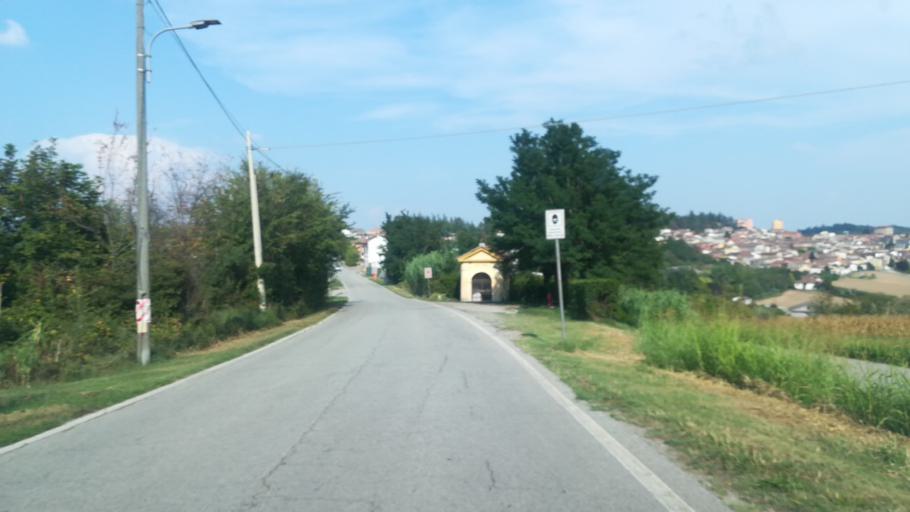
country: IT
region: Piedmont
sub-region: Provincia di Alessandria
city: San Salvatore Monferrato
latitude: 44.9965
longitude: 8.5537
